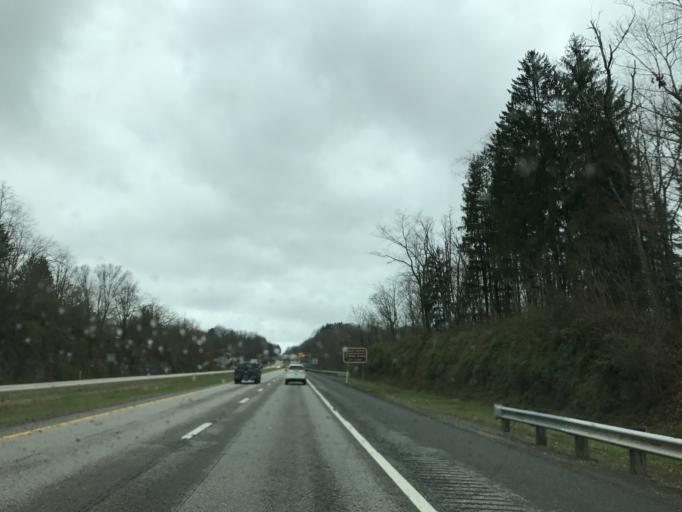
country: US
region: West Virginia
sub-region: Fayette County
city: Fayetteville
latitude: 38.0601
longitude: -81.1003
